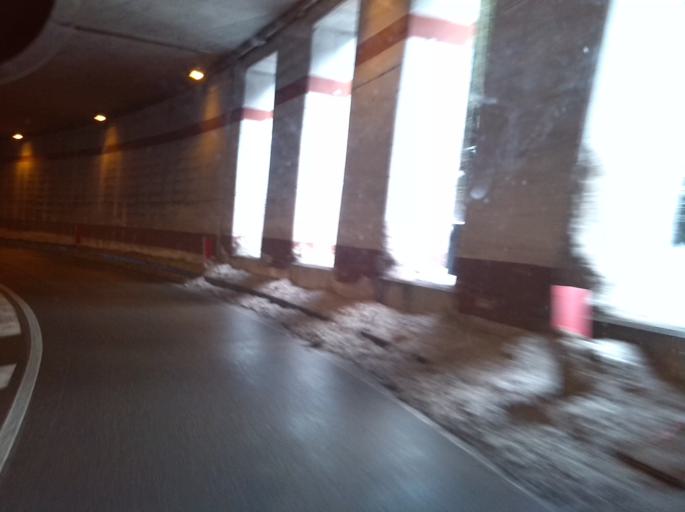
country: IT
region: Friuli Venezia Giulia
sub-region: Provincia di Udine
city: Tarvisio
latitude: 46.5025
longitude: 13.6018
